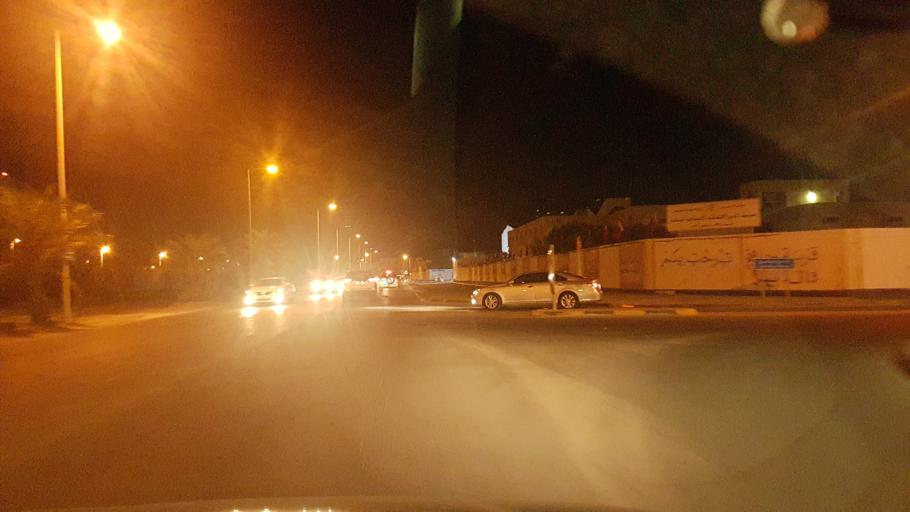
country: BH
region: Muharraq
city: Al Muharraq
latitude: 26.2802
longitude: 50.6295
